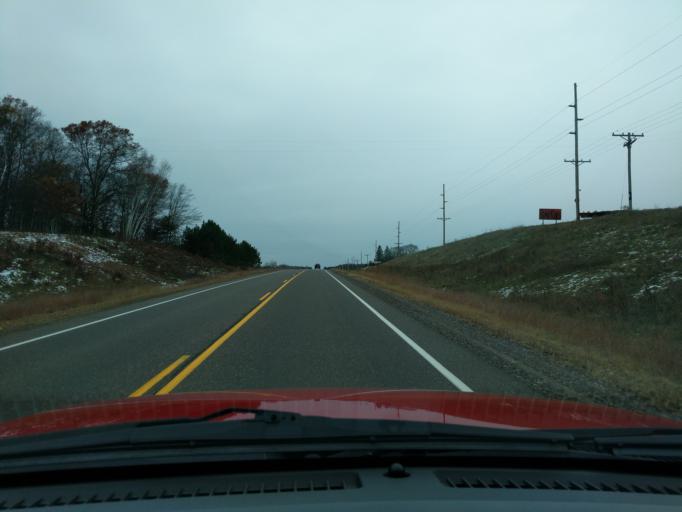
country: US
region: Wisconsin
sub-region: Washburn County
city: Shell Lake
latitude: 45.8153
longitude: -92.0698
